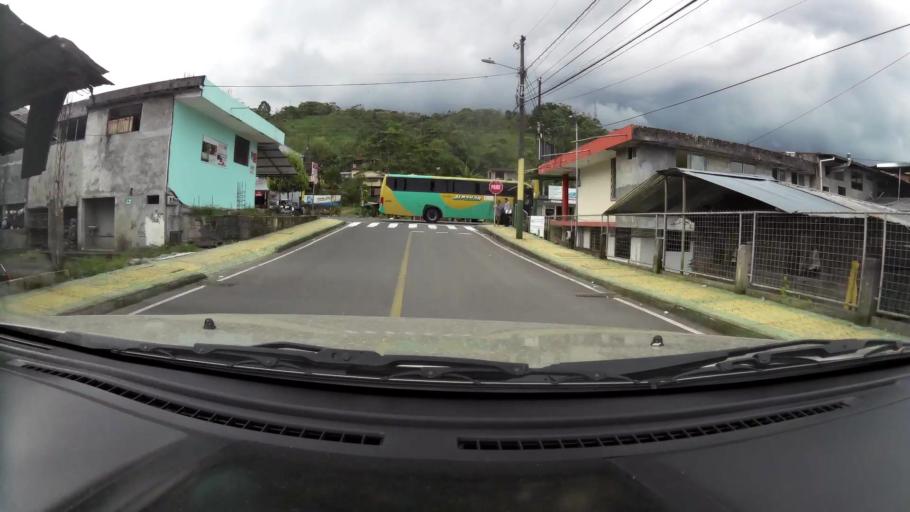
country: EC
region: Pastaza
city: Puyo
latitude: -1.4985
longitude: -78.0212
